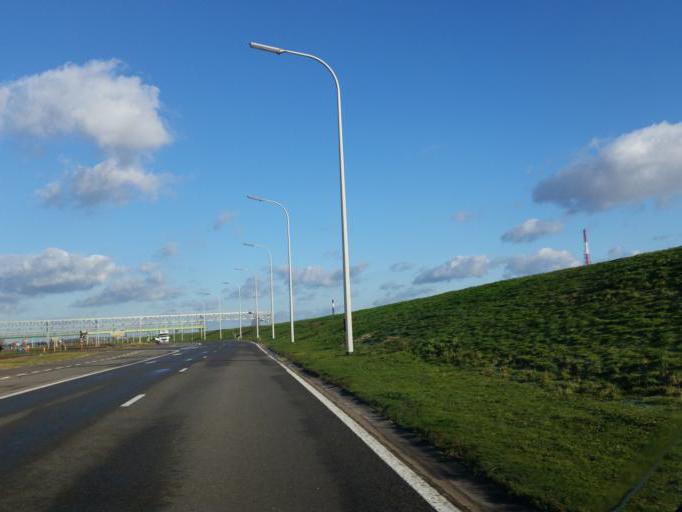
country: BE
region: Flanders
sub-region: Provincie Antwerpen
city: Zwijndrecht
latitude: 51.2695
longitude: 4.2989
